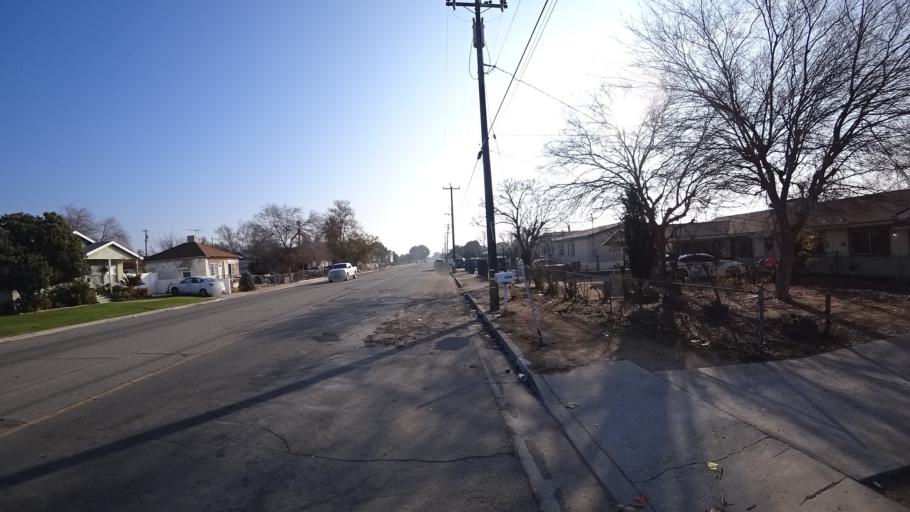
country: US
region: California
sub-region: Kern County
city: Bakersfield
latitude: 35.3744
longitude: -118.9740
